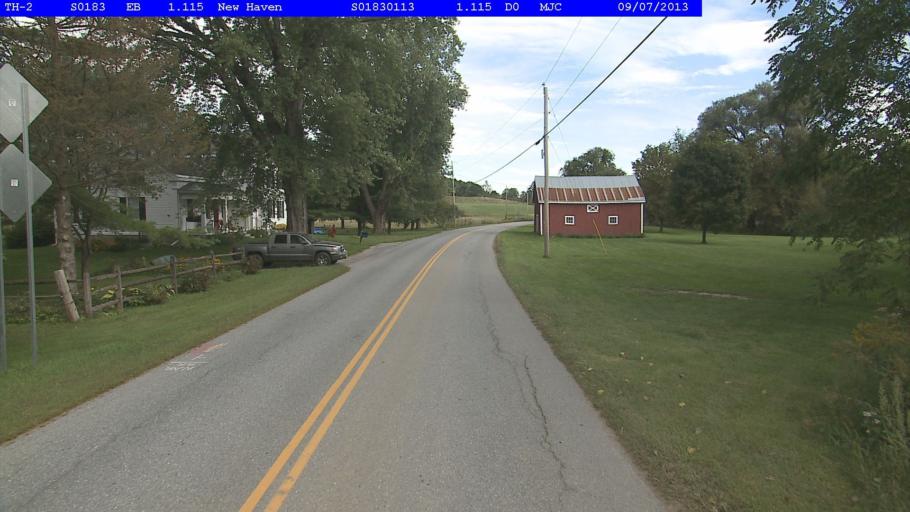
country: US
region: Vermont
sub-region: Addison County
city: Middlebury (village)
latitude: 44.0617
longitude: -73.1483
